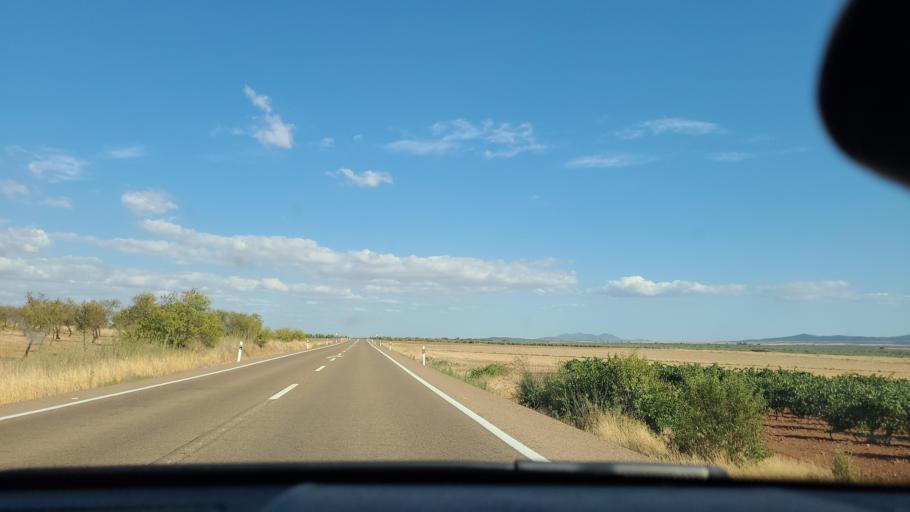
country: ES
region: Extremadura
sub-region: Provincia de Badajoz
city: Usagre
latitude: 38.3556
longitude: -6.2060
